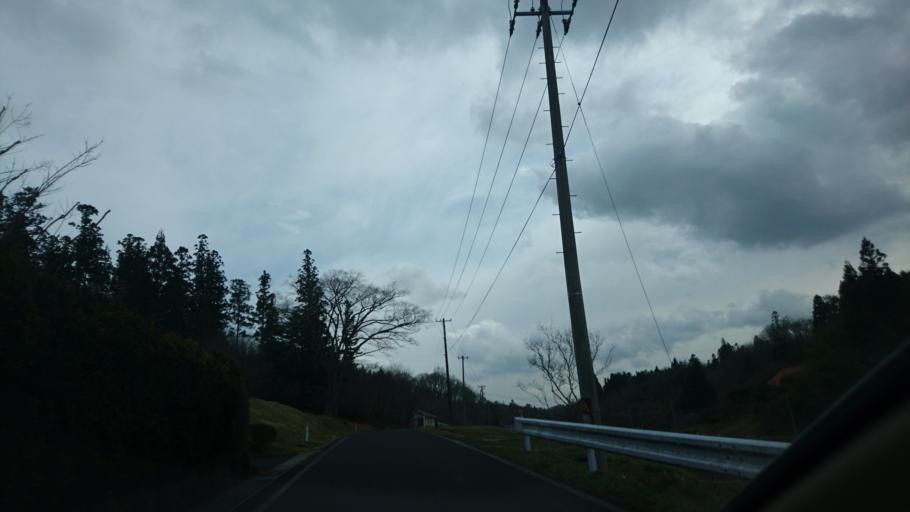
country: JP
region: Iwate
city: Ichinoseki
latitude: 38.8916
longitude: 141.1693
